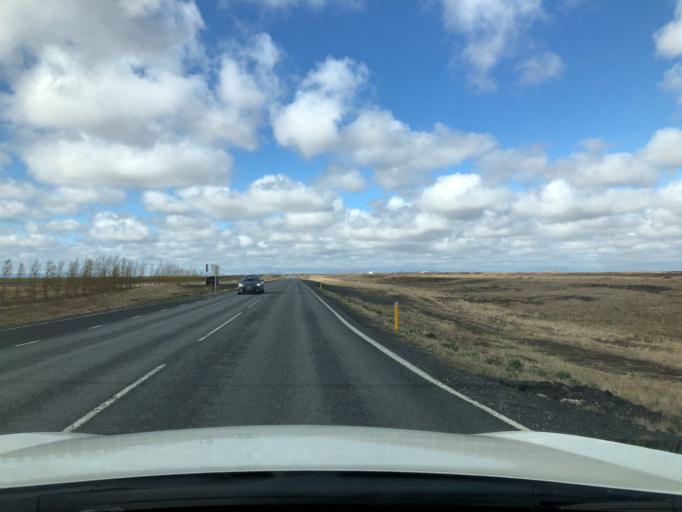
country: IS
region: South
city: Vestmannaeyjar
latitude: 63.7821
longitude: -20.2878
